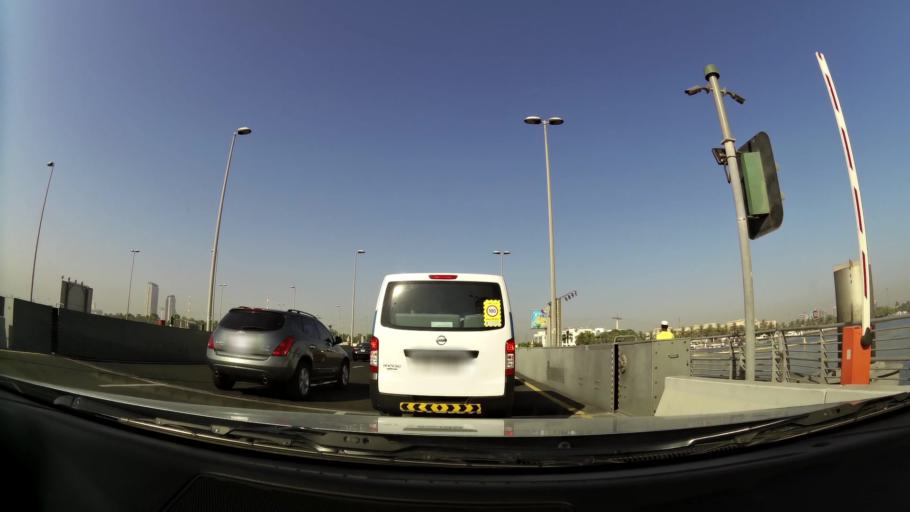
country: AE
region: Ash Shariqah
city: Sharjah
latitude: 25.2492
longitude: 55.3259
